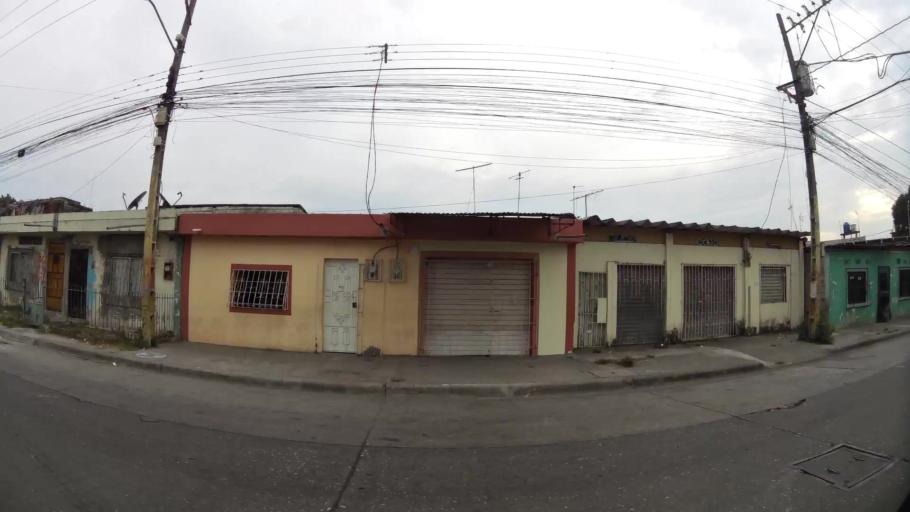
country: EC
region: Guayas
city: Guayaquil
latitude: -2.2541
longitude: -79.8743
